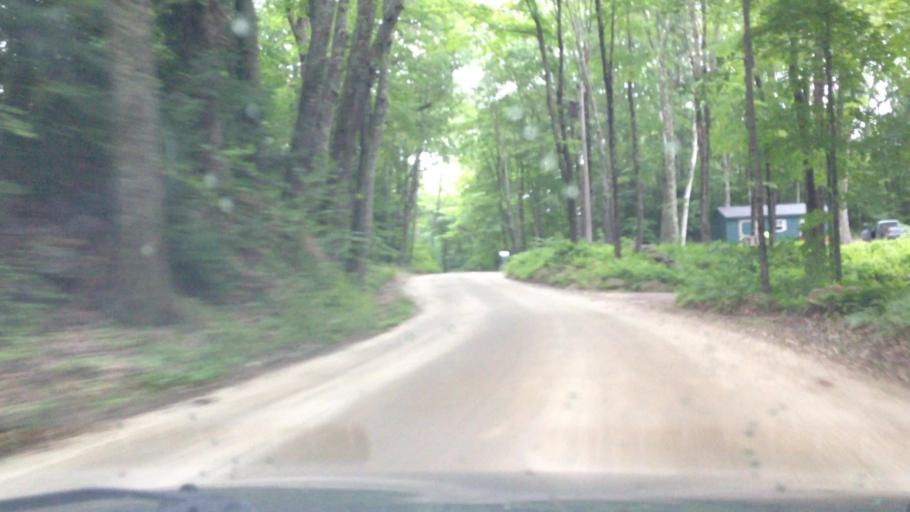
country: US
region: New Hampshire
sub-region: Cheshire County
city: Marlborough
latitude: 42.8954
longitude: -72.1879
